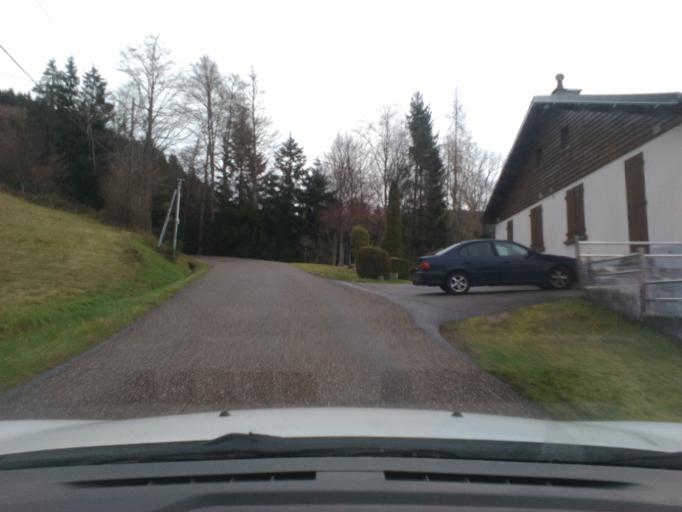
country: FR
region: Lorraine
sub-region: Departement des Vosges
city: La Bresse
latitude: 47.9727
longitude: 6.8613
